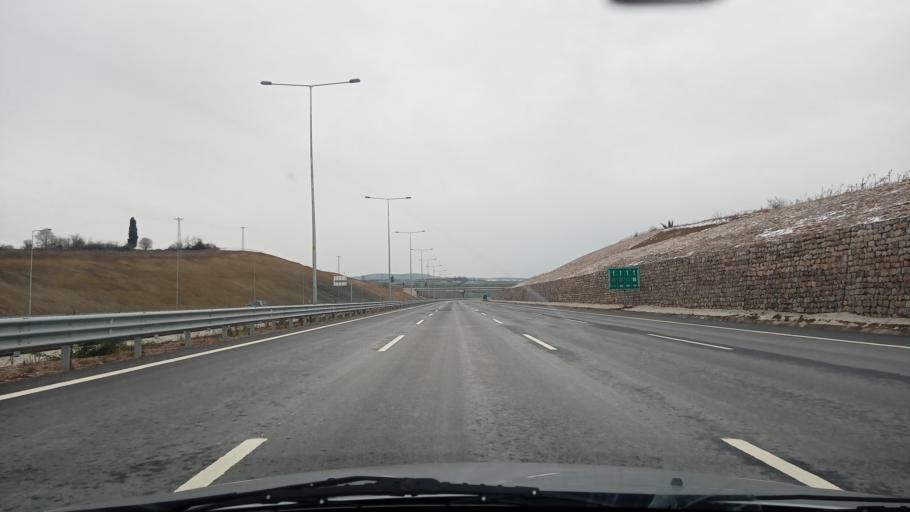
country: TR
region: Kocaeli
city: Kosekoy
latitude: 40.7946
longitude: 30.0509
